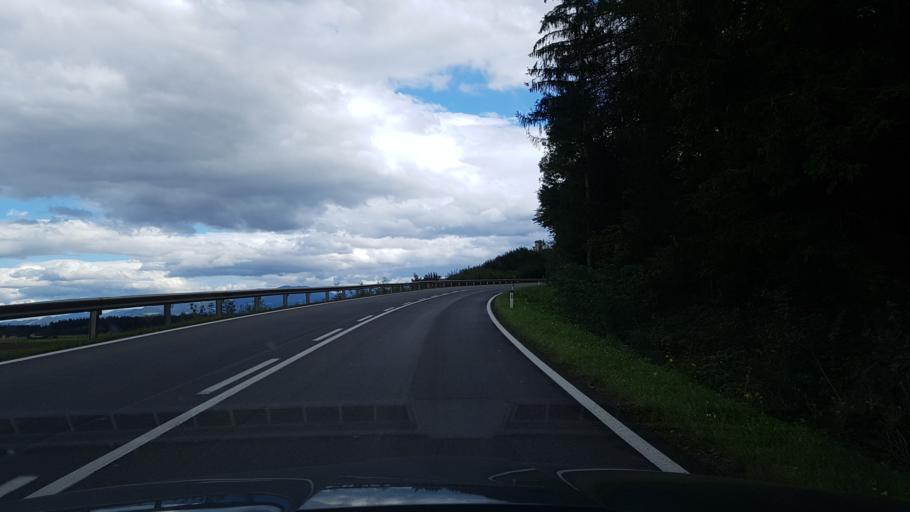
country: AT
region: Styria
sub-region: Politischer Bezirk Murtal
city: Judenburg
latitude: 47.1680
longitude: 14.6831
